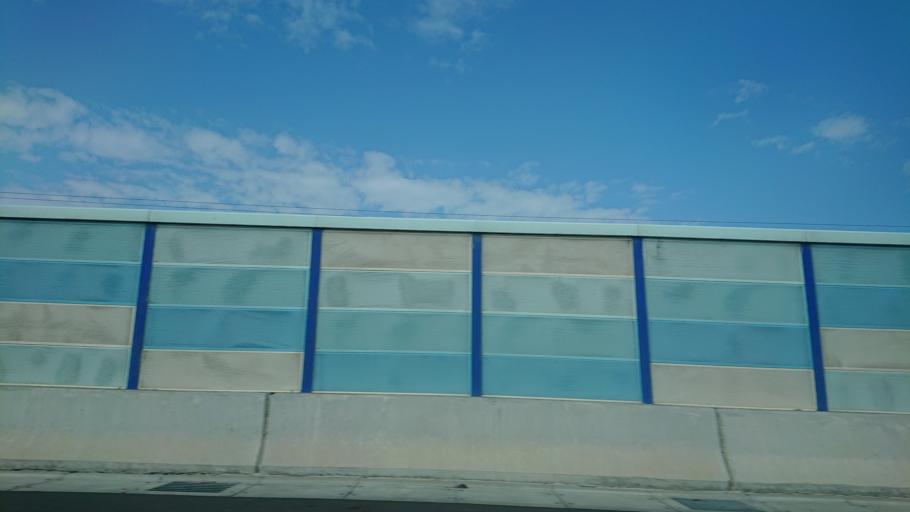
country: TW
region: Taiwan
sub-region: Changhua
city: Chang-hua
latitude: 23.9565
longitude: 120.3328
